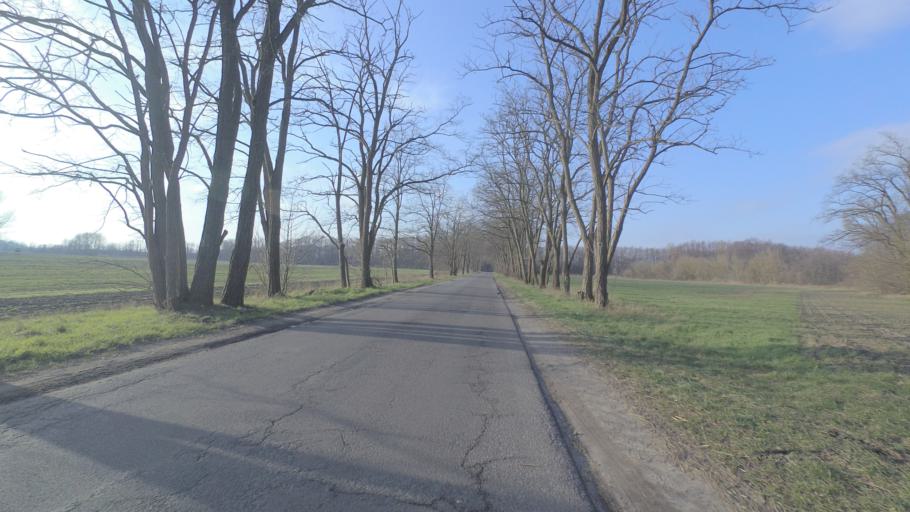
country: DE
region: Brandenburg
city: Rangsdorf
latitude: 52.2735
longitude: 13.4483
